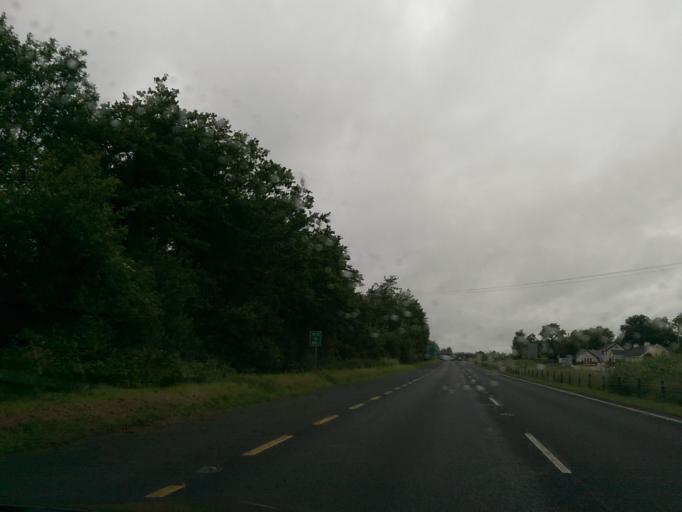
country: IE
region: Munster
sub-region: An Clar
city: Sixmilebridge
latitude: 52.6917
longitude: -8.7520
